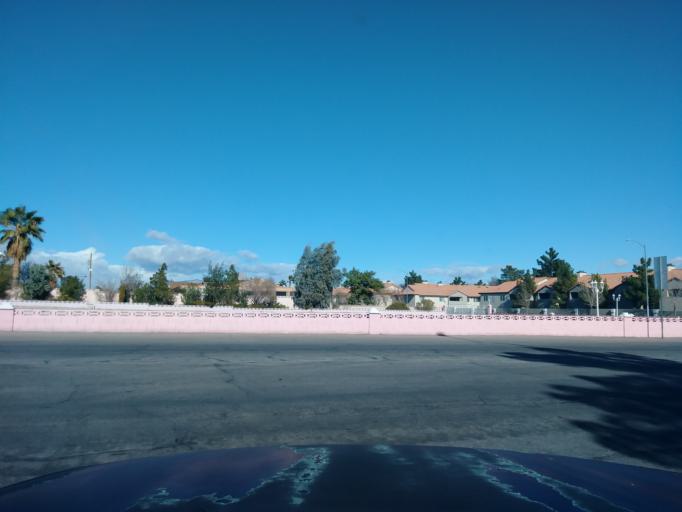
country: US
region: Nevada
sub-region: Clark County
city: Spring Valley
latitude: 36.1480
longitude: -115.2130
